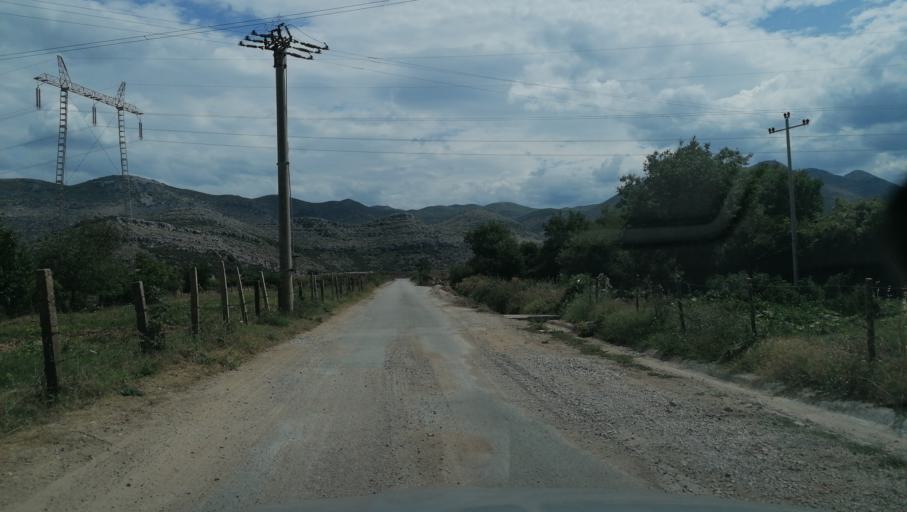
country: BA
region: Republika Srpska
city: Trebinje
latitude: 42.6681
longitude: 18.3218
